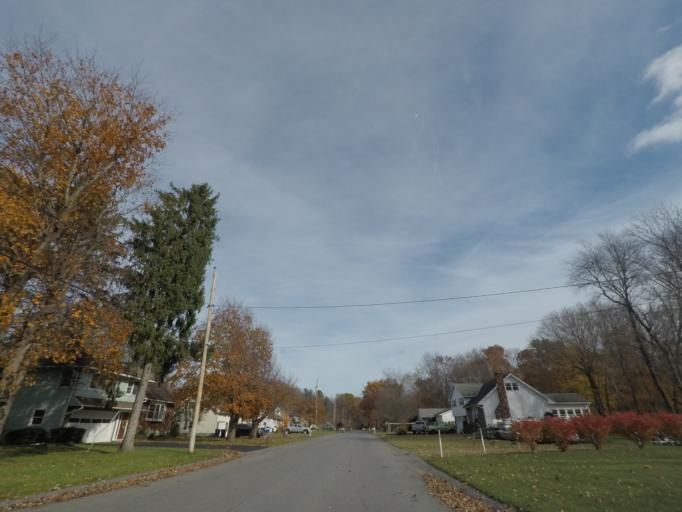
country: US
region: New York
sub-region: Schenectady County
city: Rotterdam
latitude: 42.7678
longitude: -73.9734
